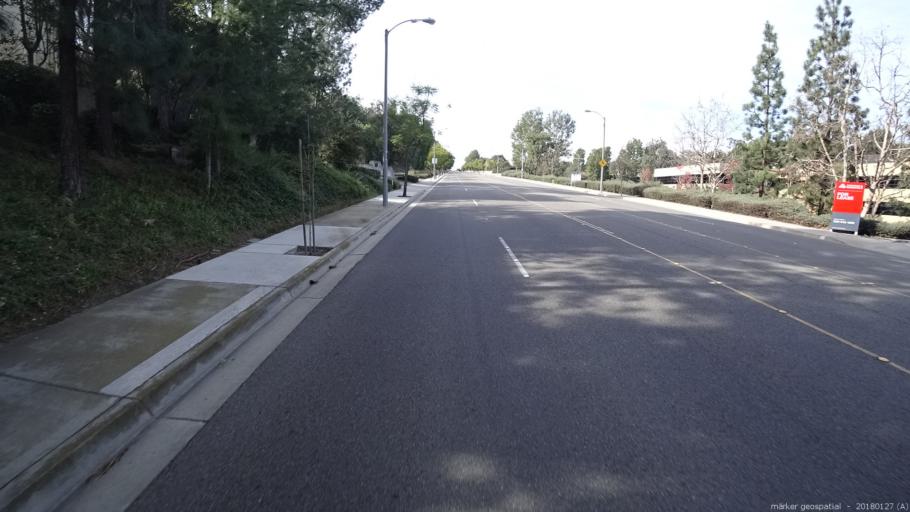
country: US
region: California
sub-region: Los Angeles County
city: Walnut
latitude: 33.9840
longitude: -117.8463
